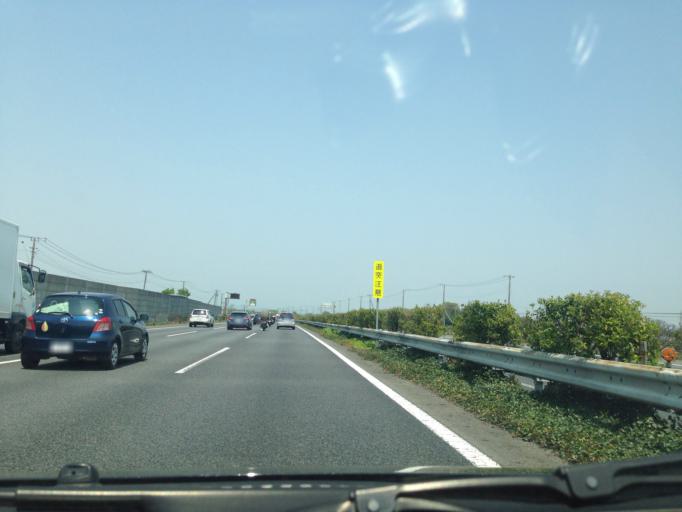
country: JP
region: Saitama
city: Hanyu
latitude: 36.1883
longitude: 139.5846
